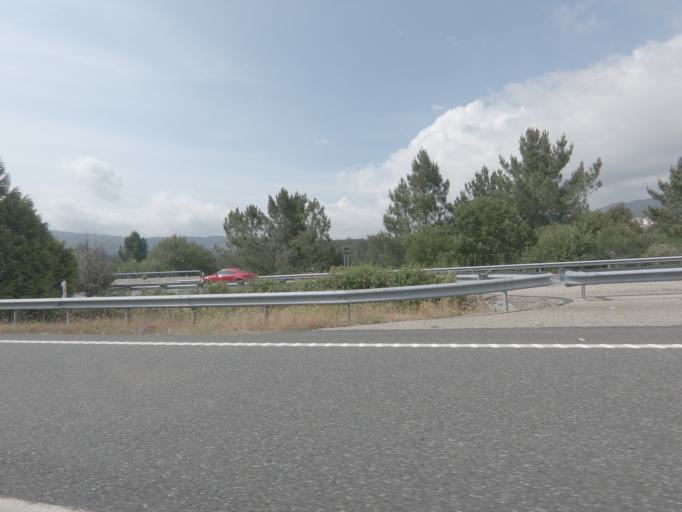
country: ES
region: Galicia
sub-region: Provincia de Pontevedra
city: Covelo
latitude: 42.2010
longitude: -8.2849
